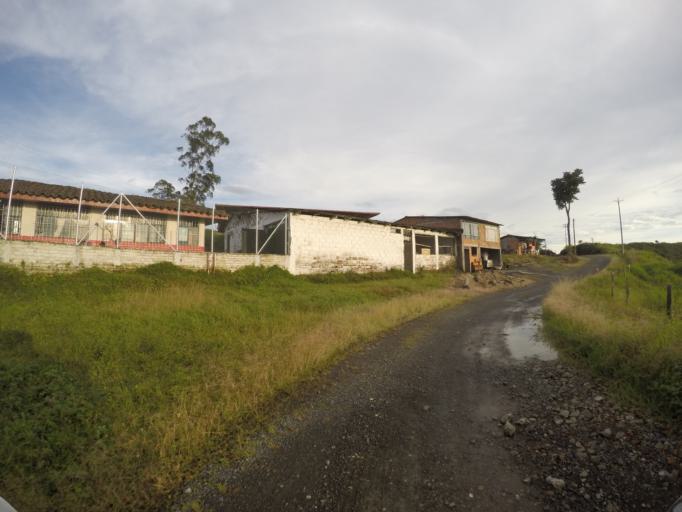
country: CO
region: Quindio
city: Filandia
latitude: 4.7267
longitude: -75.6351
